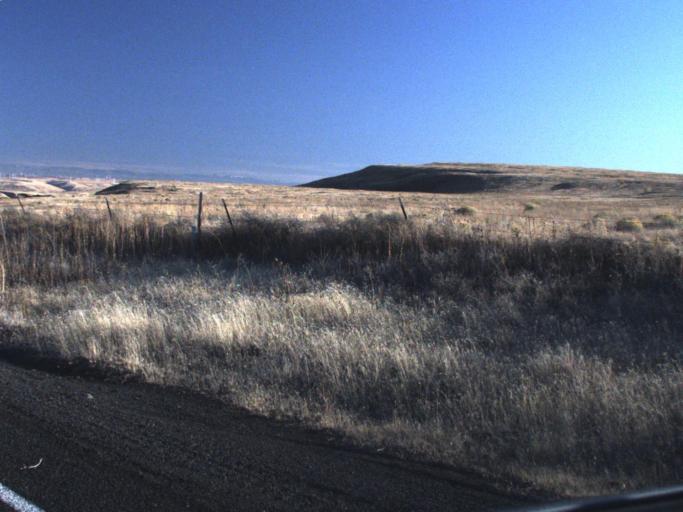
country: US
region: Washington
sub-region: Walla Walla County
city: Waitsburg
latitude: 46.6260
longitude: -118.2377
